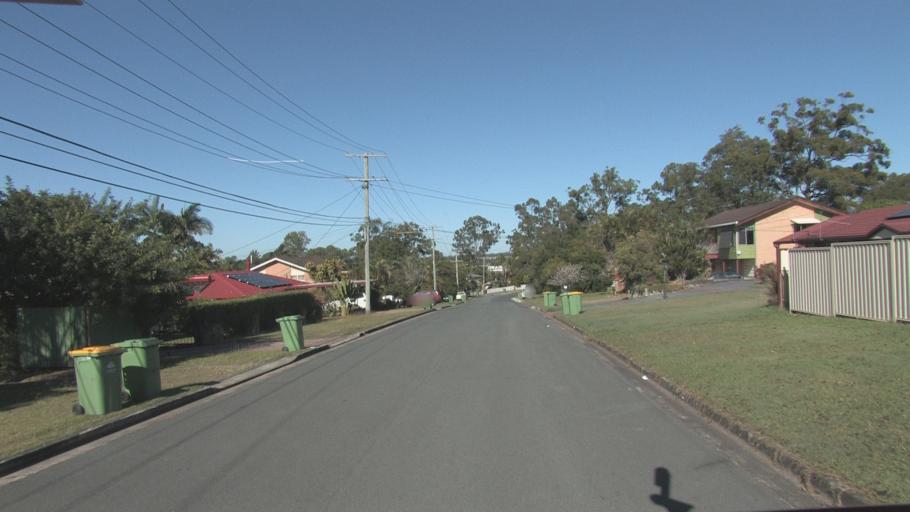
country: AU
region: Queensland
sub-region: Brisbane
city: Sunnybank Hills
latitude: -27.6564
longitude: 153.0504
